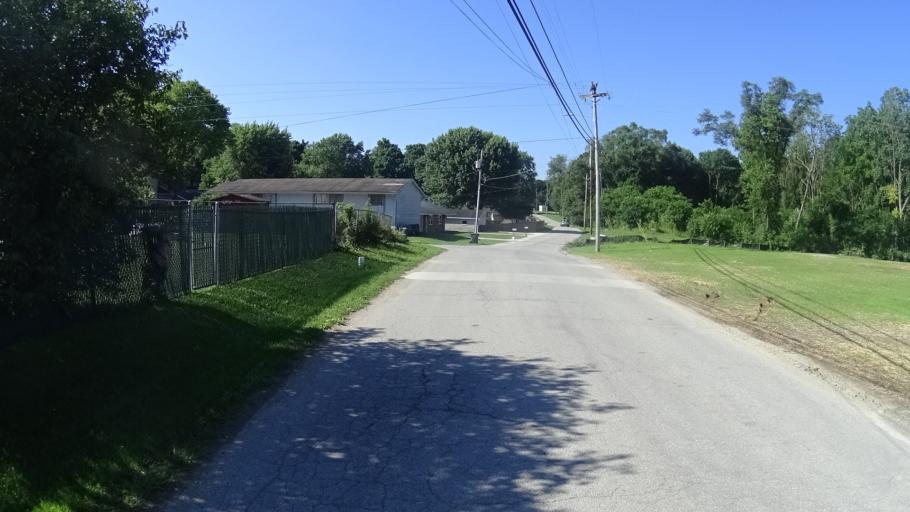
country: US
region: Indiana
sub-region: Madison County
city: Pendleton
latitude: 39.9978
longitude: -85.7473
